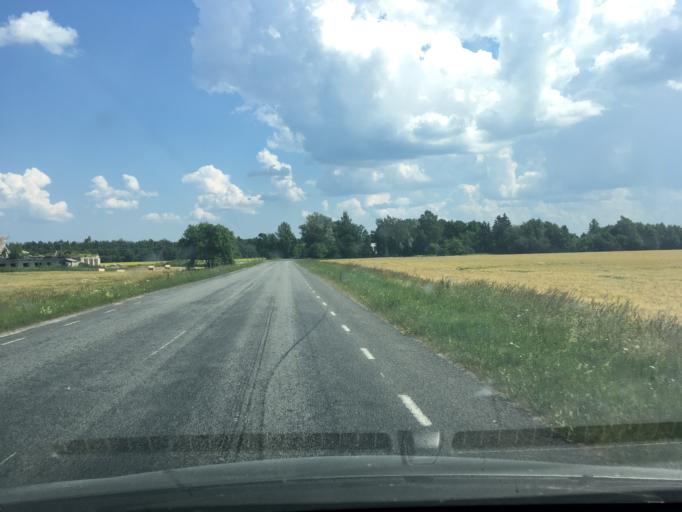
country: EE
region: Raplamaa
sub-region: Maerjamaa vald
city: Marjamaa
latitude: 58.7315
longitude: 24.2980
